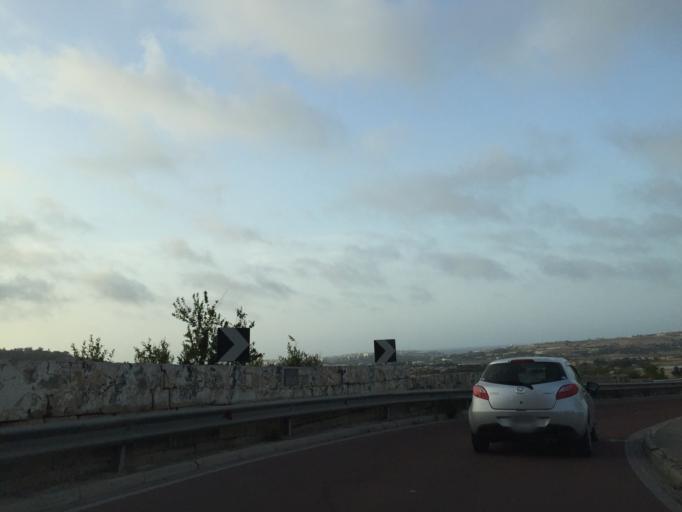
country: MT
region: Il-Mosta
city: Mosta
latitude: 35.9175
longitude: 14.4125
